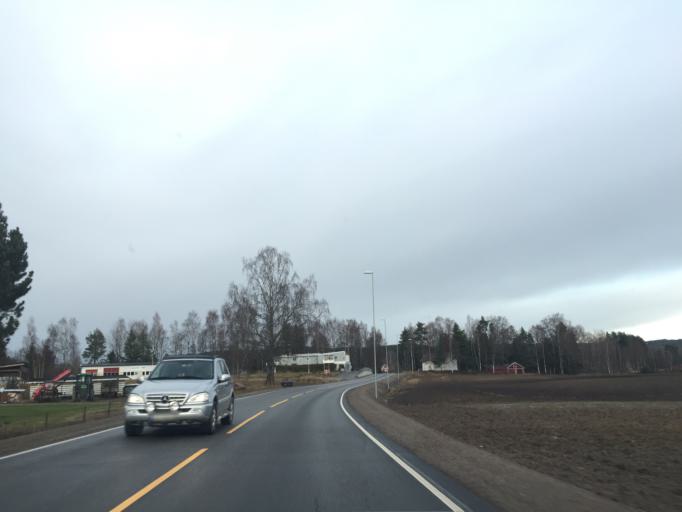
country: NO
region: Hedmark
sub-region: Grue
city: Kirkenaer
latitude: 60.5418
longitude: 12.0591
